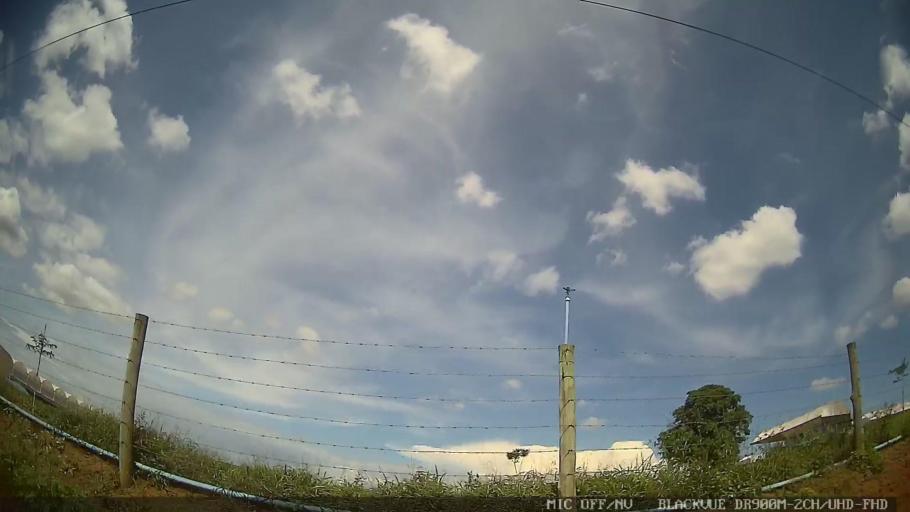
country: BR
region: Sao Paulo
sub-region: Artur Nogueira
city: Artur Nogueira
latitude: -22.5890
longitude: -47.0749
